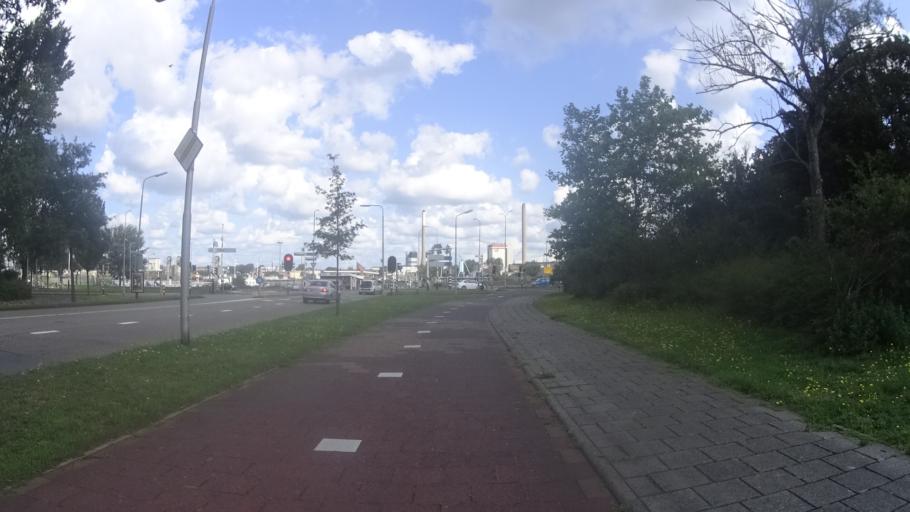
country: NL
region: North Holland
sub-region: Gemeente Velsen
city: Velsen-Zuid
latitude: 52.4614
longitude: 4.6334
